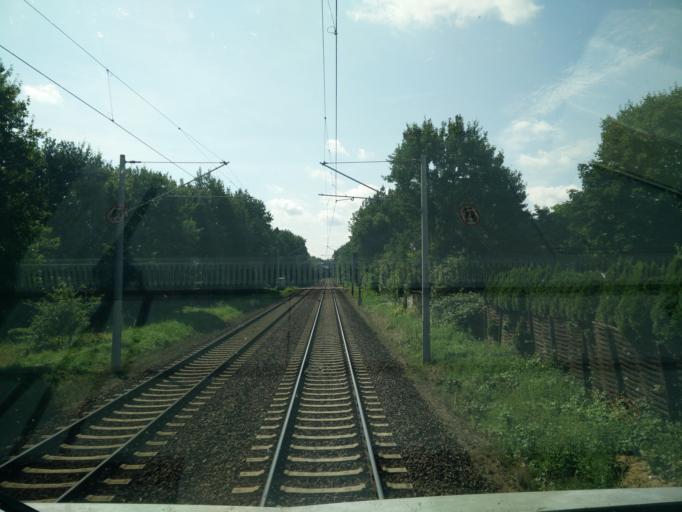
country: DE
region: Brandenburg
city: Konigs Wusterhausen
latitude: 52.2735
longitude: 13.6340
